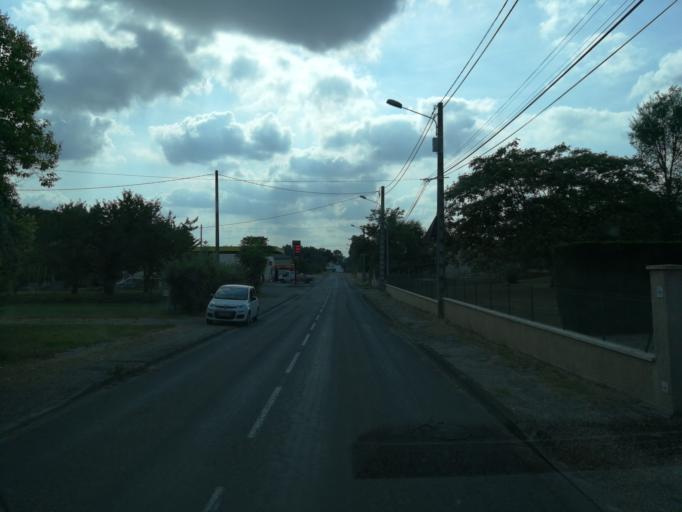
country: FR
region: Aquitaine
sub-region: Departement du Lot-et-Garonne
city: Fumel
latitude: 44.5030
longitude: 0.9587
